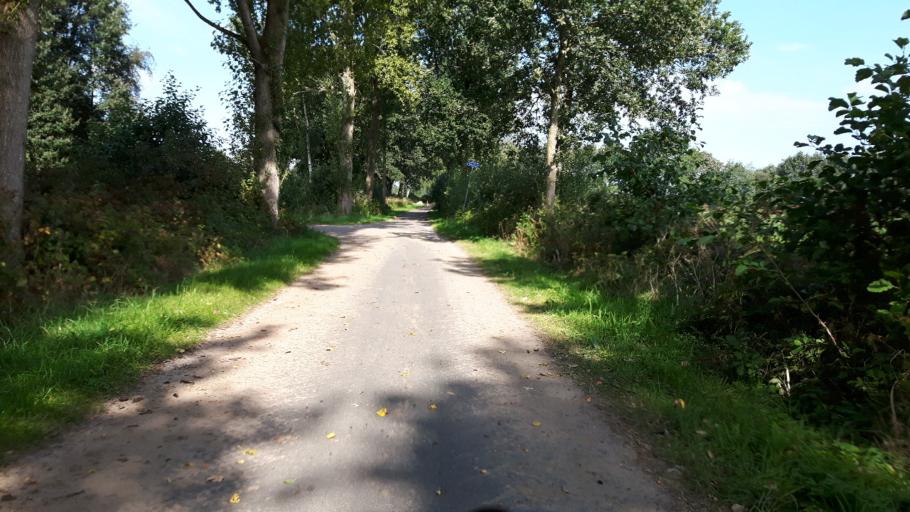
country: NL
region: Groningen
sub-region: Gemeente Leek
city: Leek
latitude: 53.1183
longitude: 6.4737
